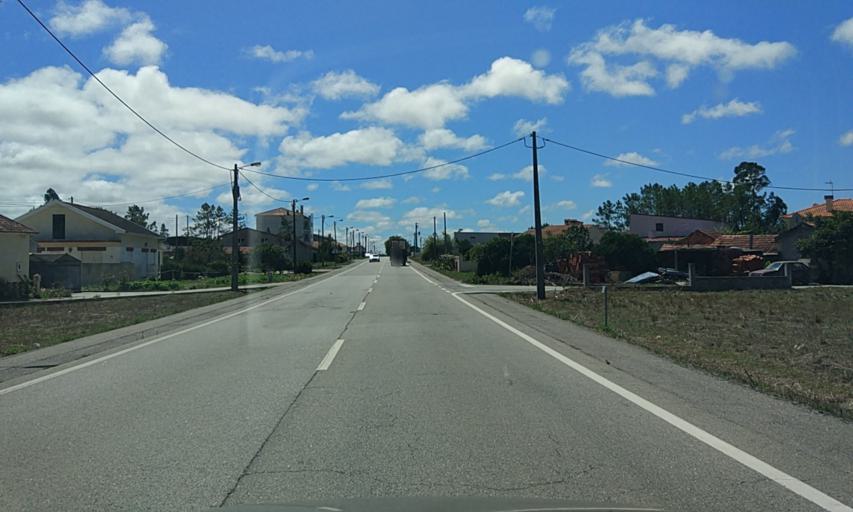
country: PT
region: Aveiro
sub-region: Vagos
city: Vagos
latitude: 40.4992
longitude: -8.6822
